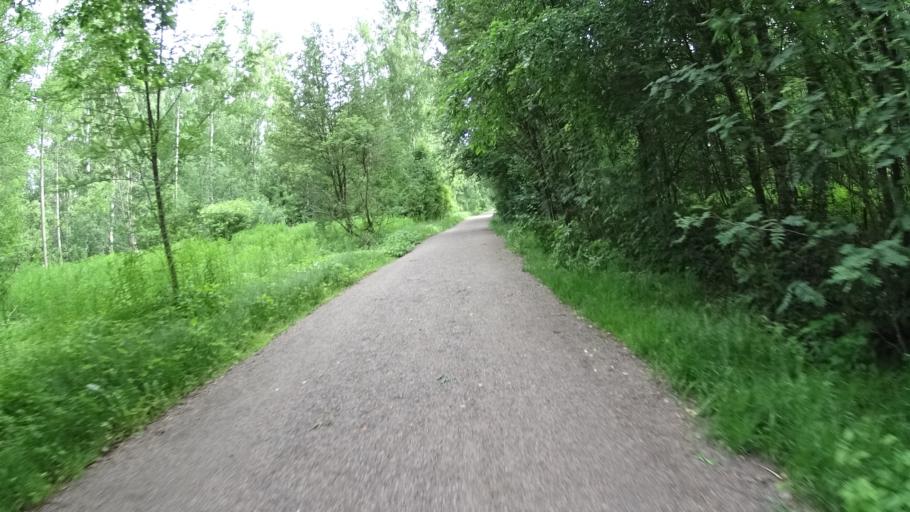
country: FI
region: Uusimaa
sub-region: Helsinki
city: Kilo
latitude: 60.1860
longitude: 24.7729
